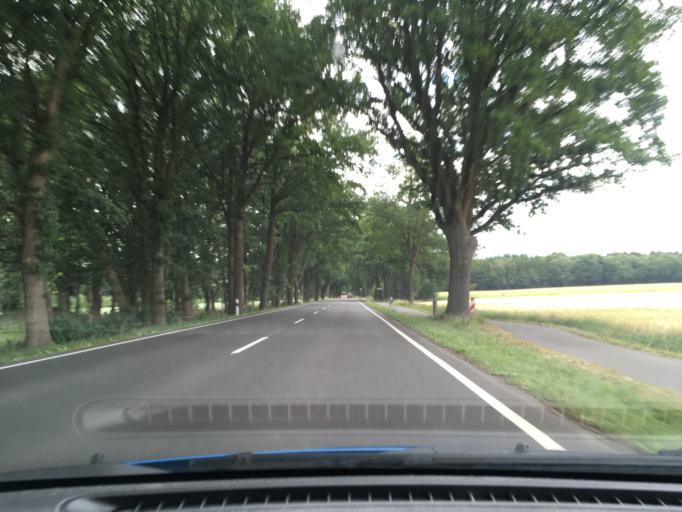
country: DE
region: Lower Saxony
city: Drestedt
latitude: 53.3349
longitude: 9.8122
